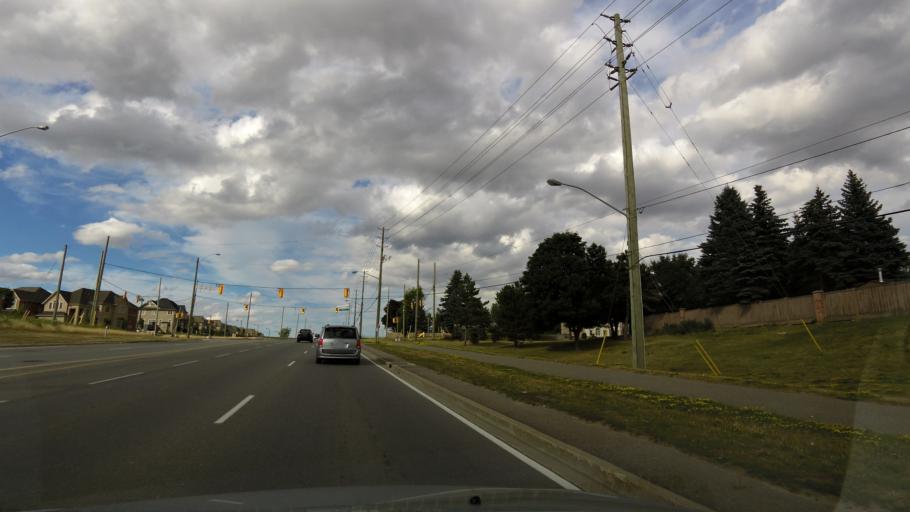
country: CA
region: Ontario
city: Brampton
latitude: 43.7400
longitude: -79.8183
